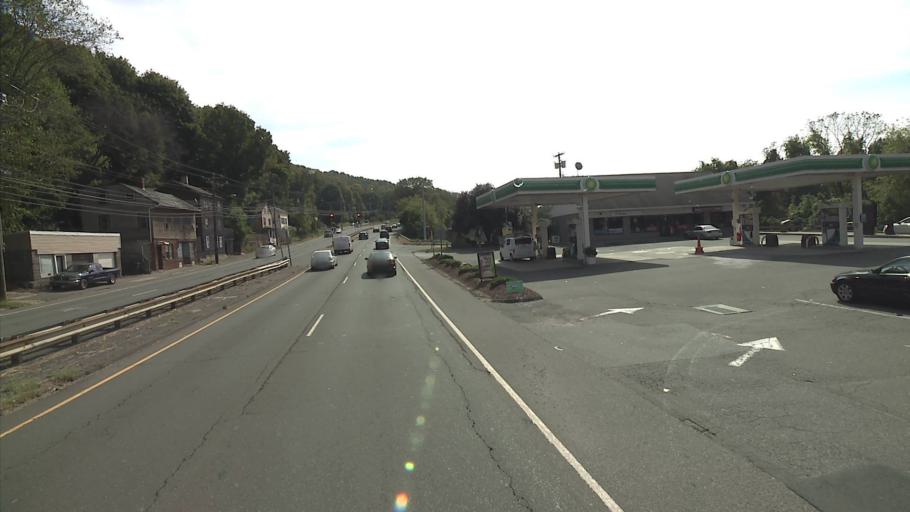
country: US
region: Connecticut
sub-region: New Haven County
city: Derby
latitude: 41.3146
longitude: -73.0792
